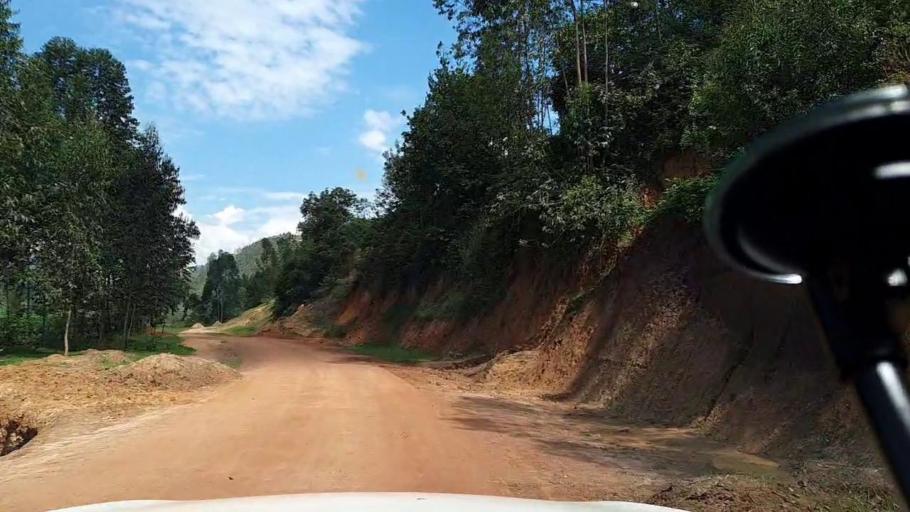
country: RW
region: Kigali
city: Kigali
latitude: -1.7928
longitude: 29.8865
